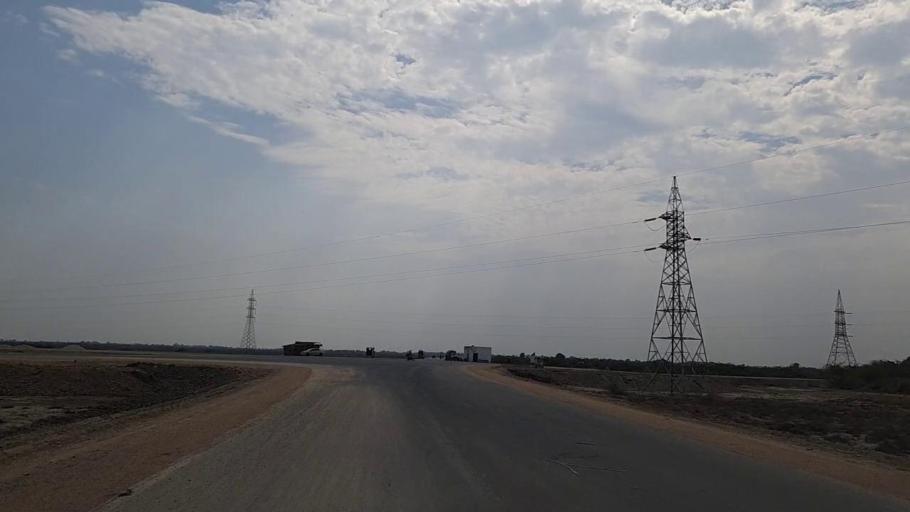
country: PK
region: Sindh
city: Naukot
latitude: 24.9545
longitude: 69.2827
